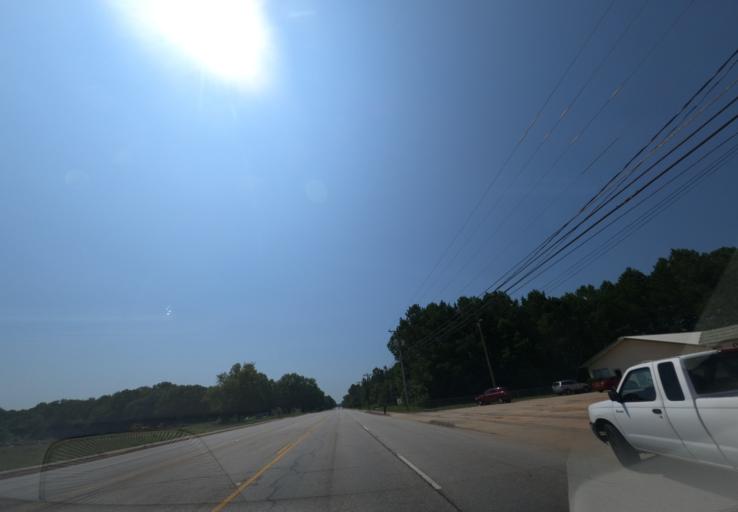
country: US
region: South Carolina
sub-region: Greenwood County
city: Greenwood
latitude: 34.1477
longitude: -82.1360
